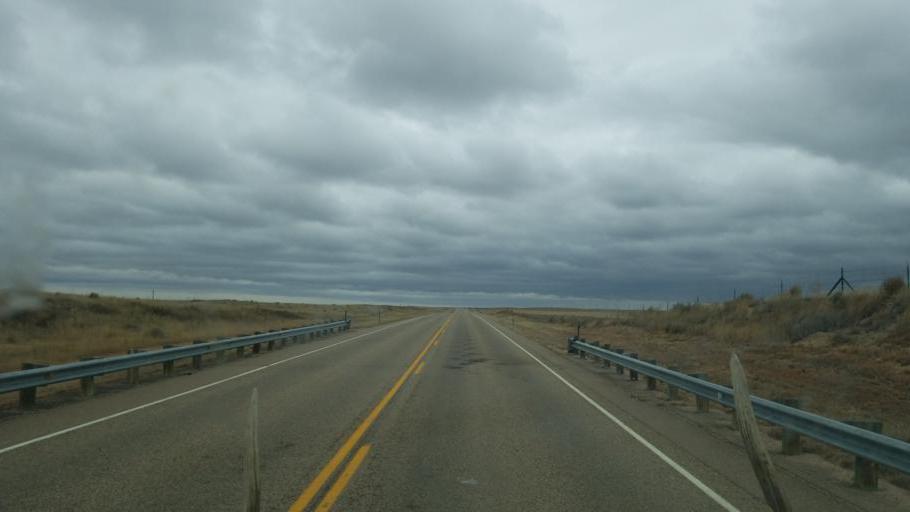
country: US
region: Colorado
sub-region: Kiowa County
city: Eads
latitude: 38.7888
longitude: -102.6811
